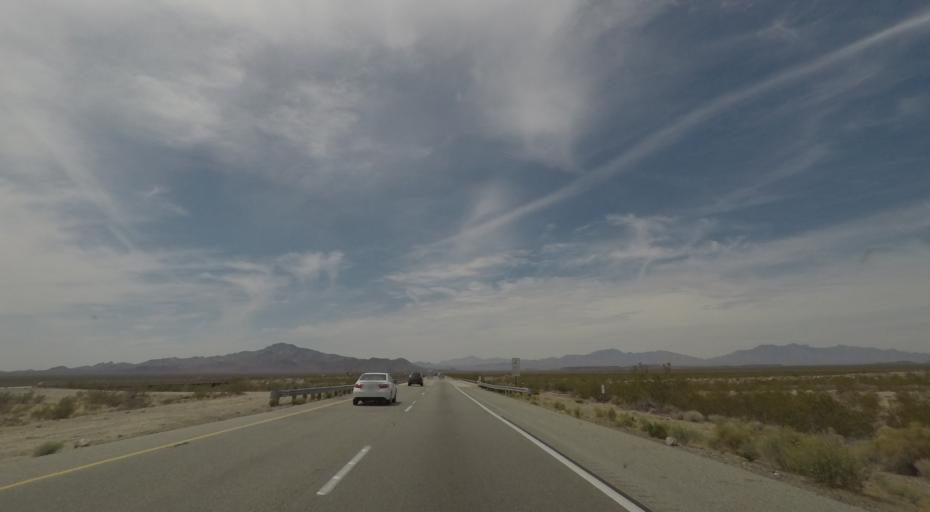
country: US
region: California
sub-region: San Bernardino County
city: Needles
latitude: 34.8088
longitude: -115.2287
